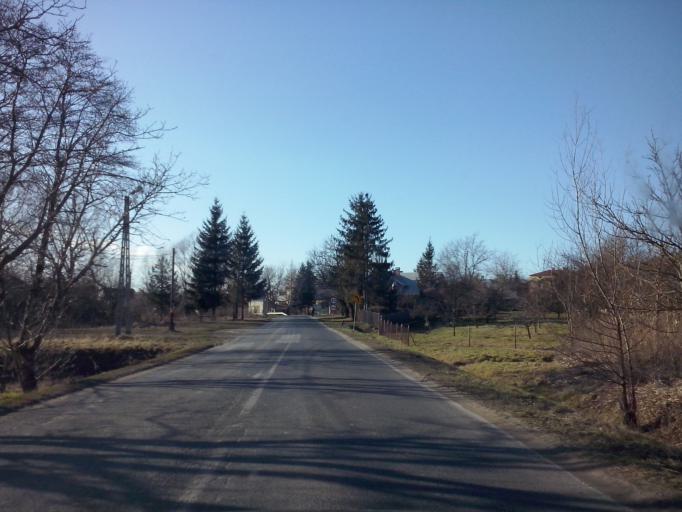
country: PL
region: Subcarpathian Voivodeship
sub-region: Powiat nizanski
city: Krzeszow
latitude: 50.4035
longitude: 22.3453
